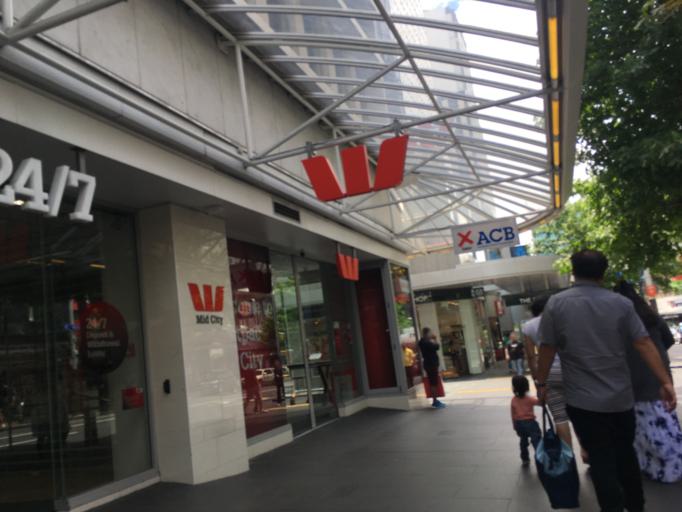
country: NZ
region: Auckland
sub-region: Auckland
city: Auckland
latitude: -36.8499
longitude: 174.7652
